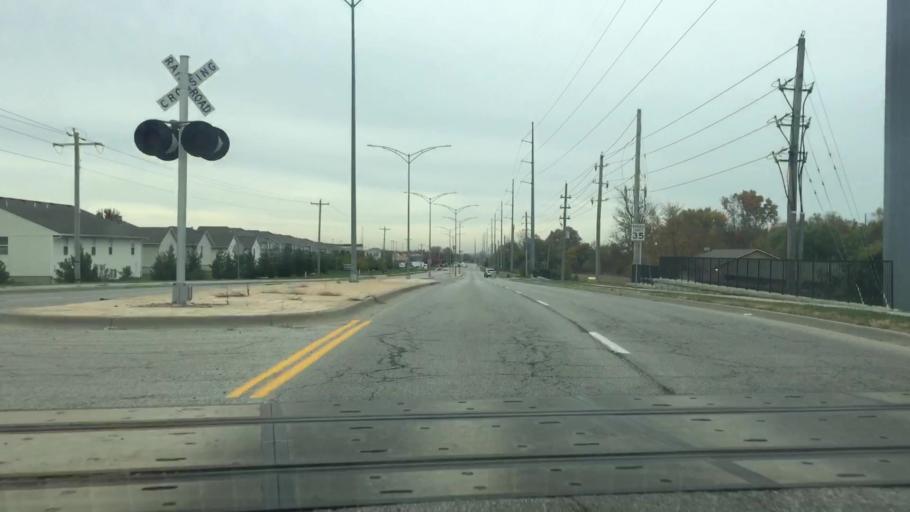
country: US
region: Missouri
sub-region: Cass County
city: Belton
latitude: 38.8079
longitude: -94.5125
